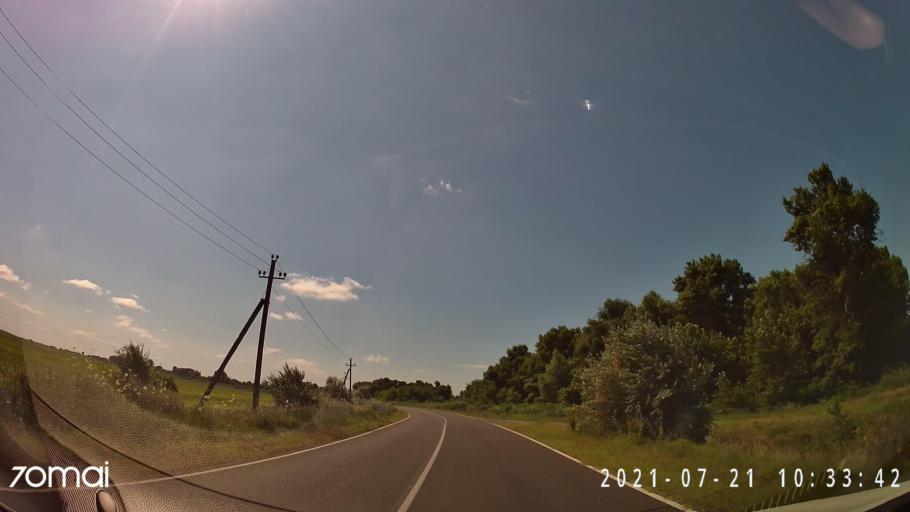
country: RO
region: Tulcea
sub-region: Oras Isaccea
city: Isaccea
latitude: 45.3003
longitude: 28.4370
